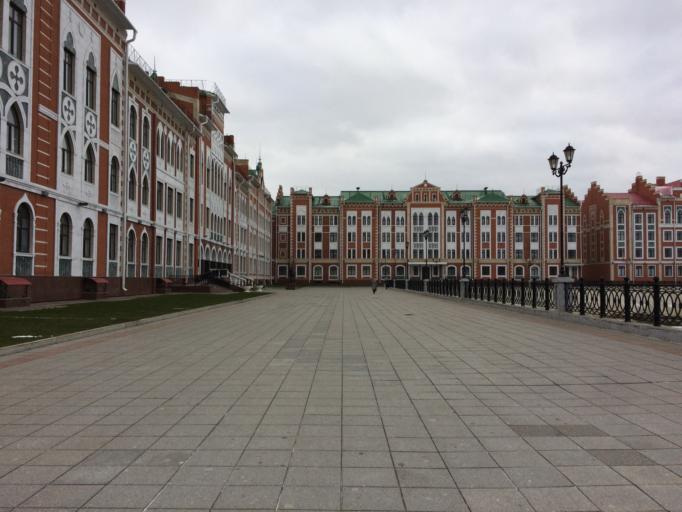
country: RU
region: Mariy-El
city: Yoshkar-Ola
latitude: 56.6367
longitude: 47.9096
